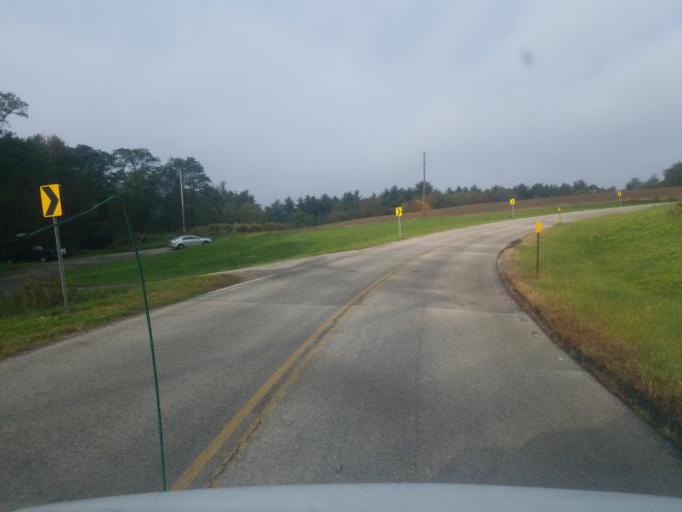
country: US
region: Ohio
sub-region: Richland County
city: Ontario
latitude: 40.7151
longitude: -82.6325
